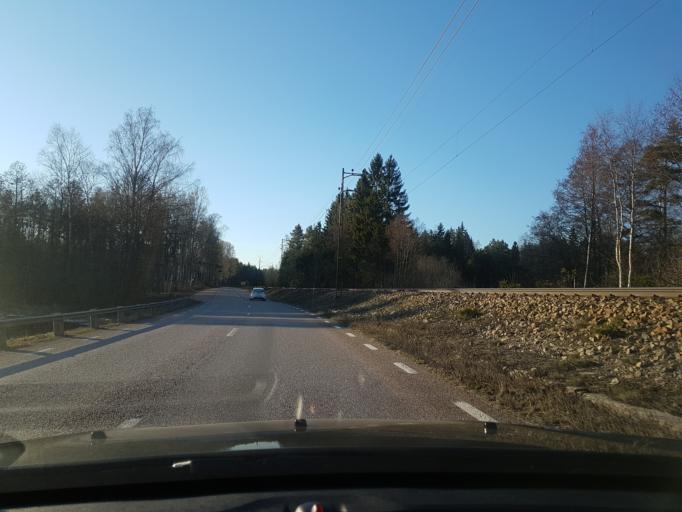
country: SE
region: Vaestmanland
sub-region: Sala Kommun
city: Sala
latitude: 59.9625
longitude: 16.5122
